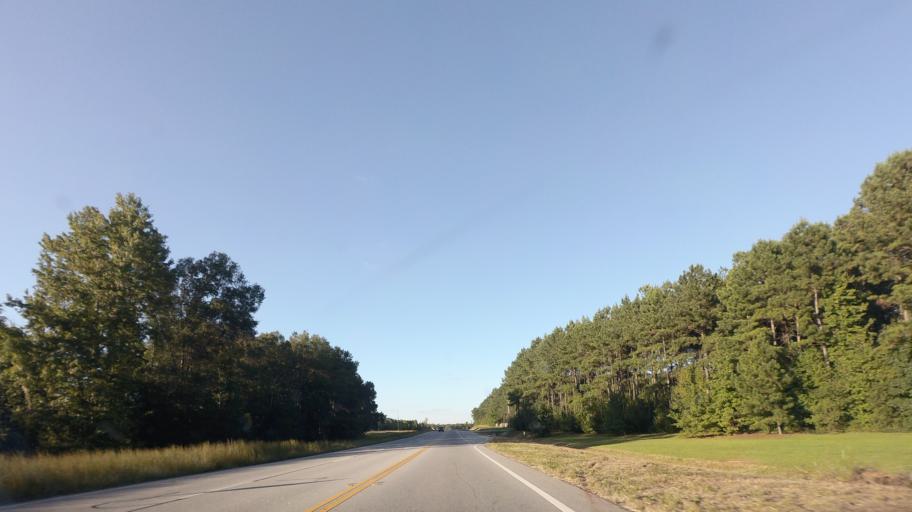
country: US
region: Georgia
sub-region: Spalding County
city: East Griffin
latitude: 33.2851
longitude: -84.1989
